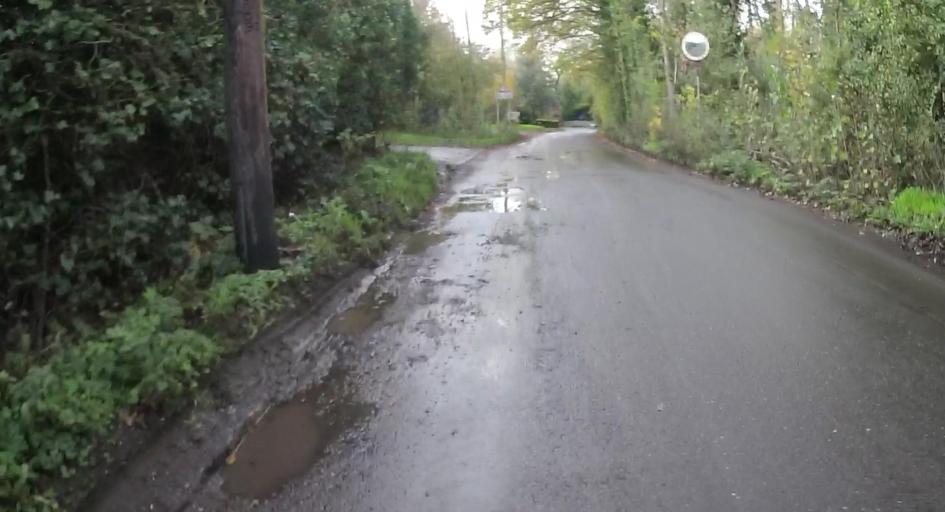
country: GB
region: England
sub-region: West Berkshire
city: Arborfield
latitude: 51.4039
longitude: -0.9101
